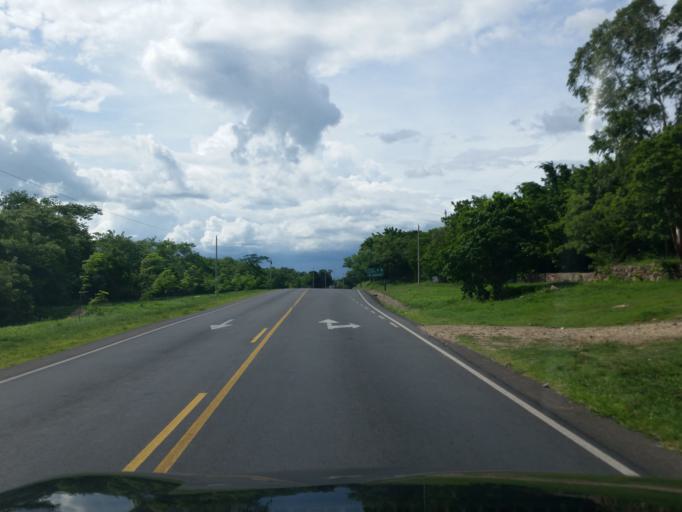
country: NI
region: Matagalpa
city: Ciudad Dario
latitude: 12.7487
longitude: -86.1221
